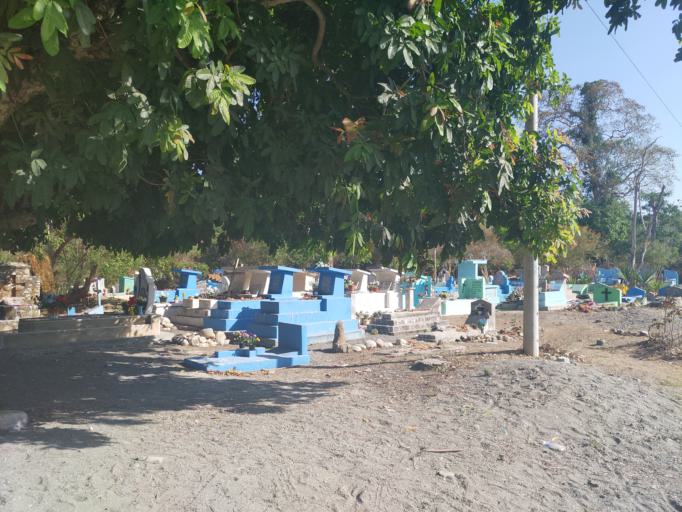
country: TL
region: Viqueque
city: Viqueque
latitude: -8.9736
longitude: 126.0534
